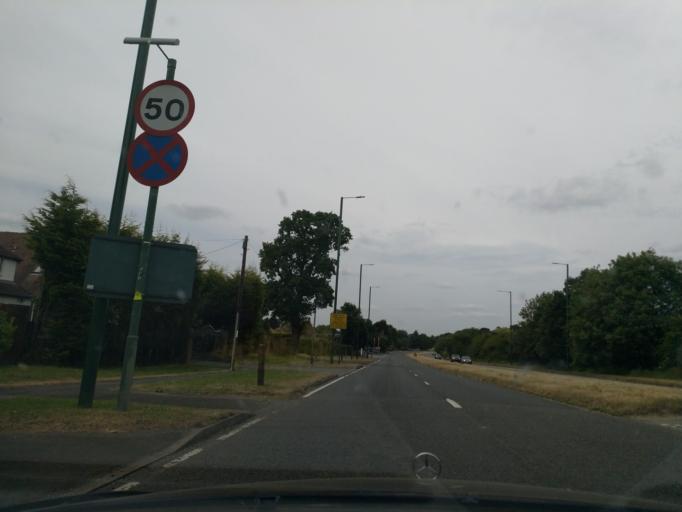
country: GB
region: England
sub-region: Solihull
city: Balsall Common
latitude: 52.4004
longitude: -1.6560
